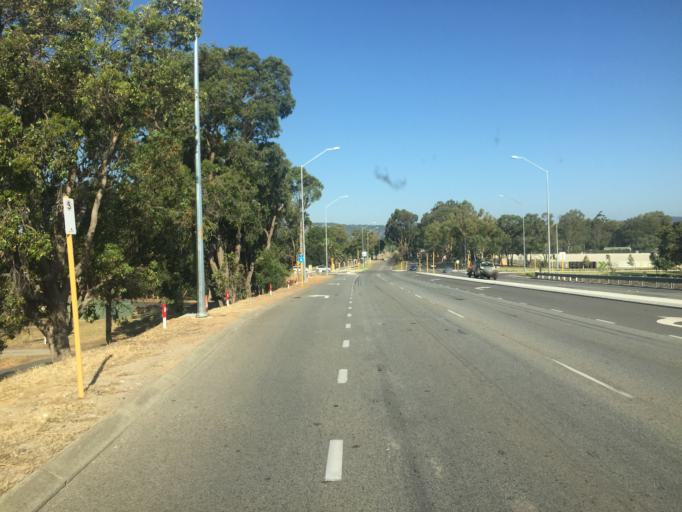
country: AU
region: Western Australia
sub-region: Canning
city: East Cannington
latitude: -32.0047
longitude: 115.9787
